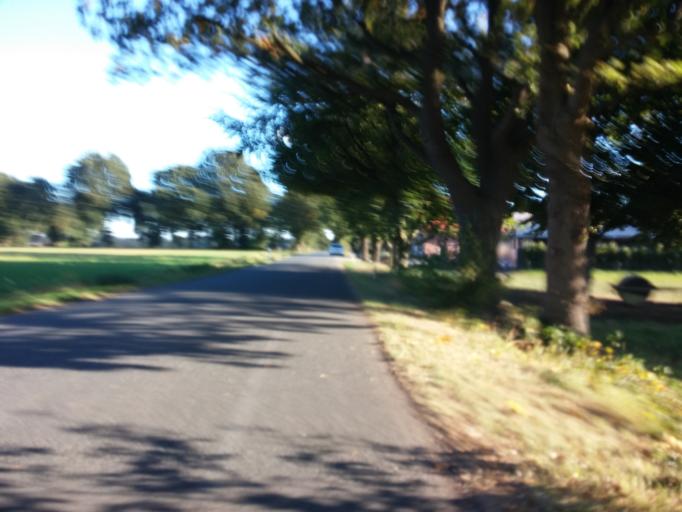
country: DE
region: North Rhine-Westphalia
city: Dorsten
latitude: 51.6472
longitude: 6.9930
